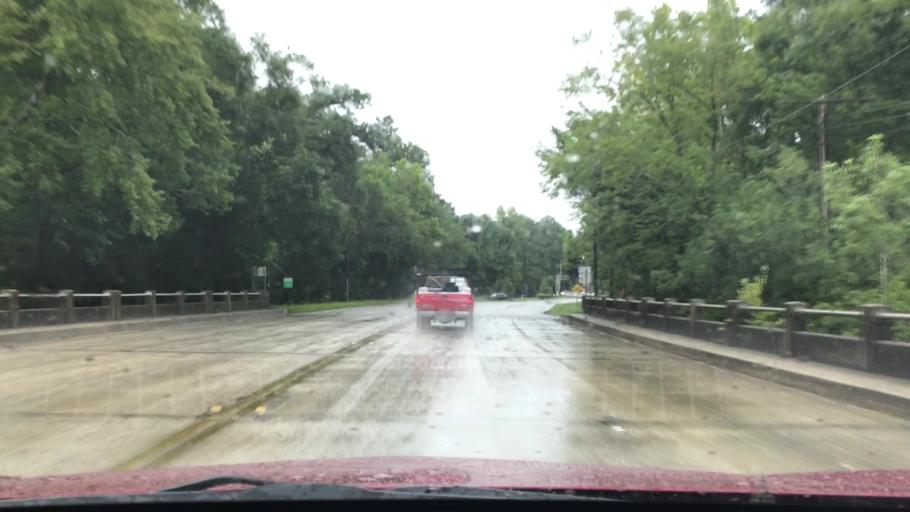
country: US
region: South Carolina
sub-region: Horry County
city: Conway
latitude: 33.8372
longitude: -79.0450
